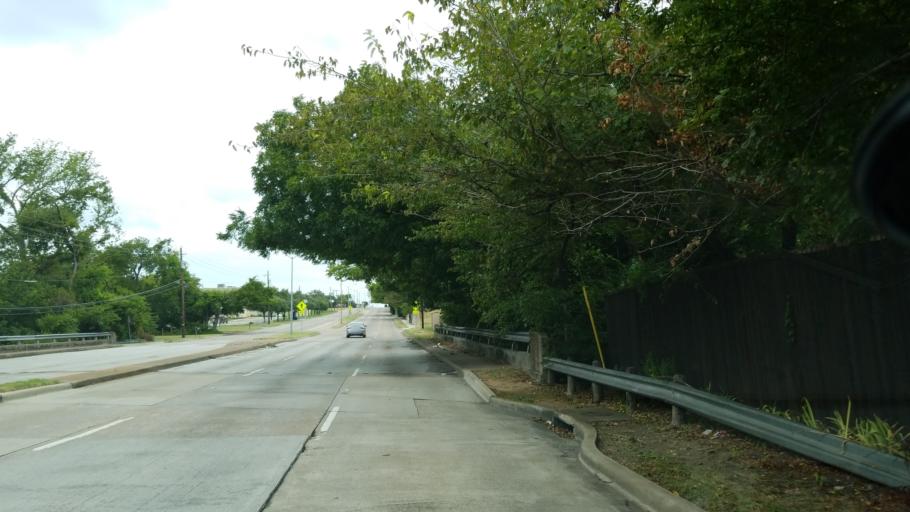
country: US
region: Texas
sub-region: Dallas County
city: Duncanville
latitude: 32.6635
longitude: -96.8570
